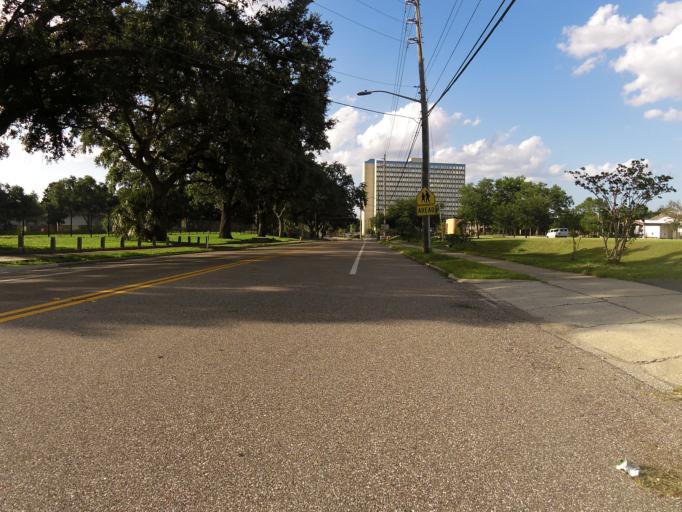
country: US
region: Florida
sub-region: Duval County
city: Jacksonville
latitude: 30.3386
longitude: -81.6634
